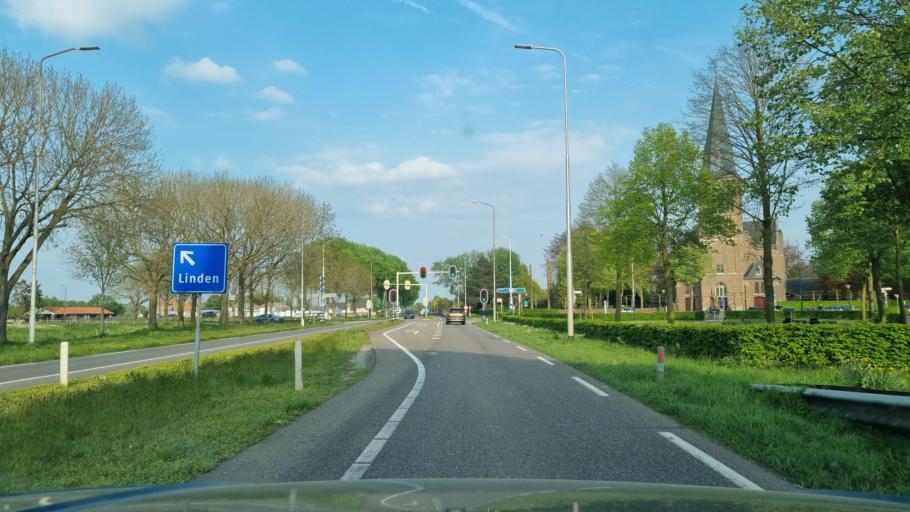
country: NL
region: North Brabant
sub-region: Gemeente Cuijk
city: Cuijk
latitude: 51.7265
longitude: 5.8246
